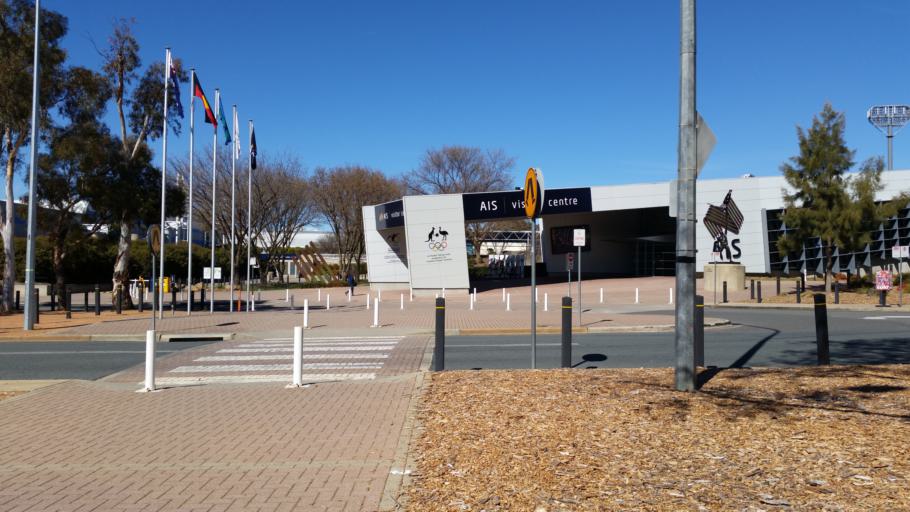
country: AU
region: Australian Capital Territory
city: Kaleen
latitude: -35.2466
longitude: 149.1010
